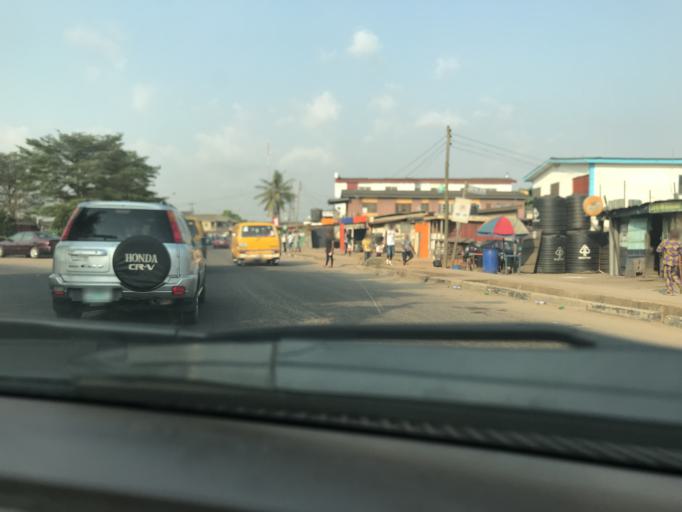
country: NG
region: Lagos
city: Ikotun
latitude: 6.5762
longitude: 3.2814
